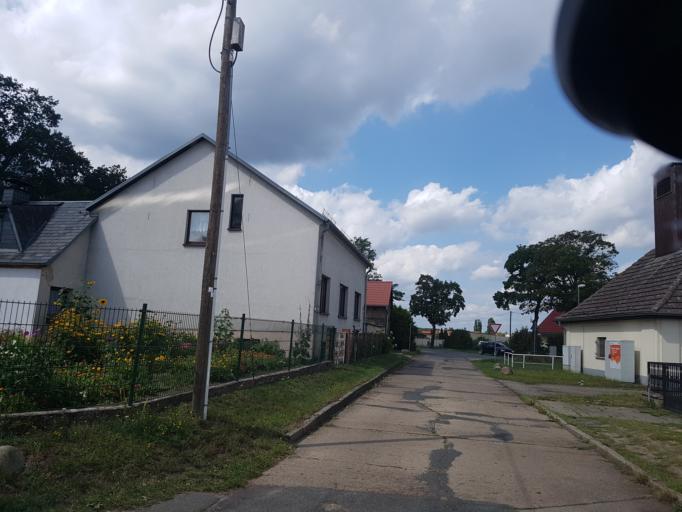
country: DE
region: Brandenburg
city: Borkwalde
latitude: 52.2860
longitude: 12.8368
